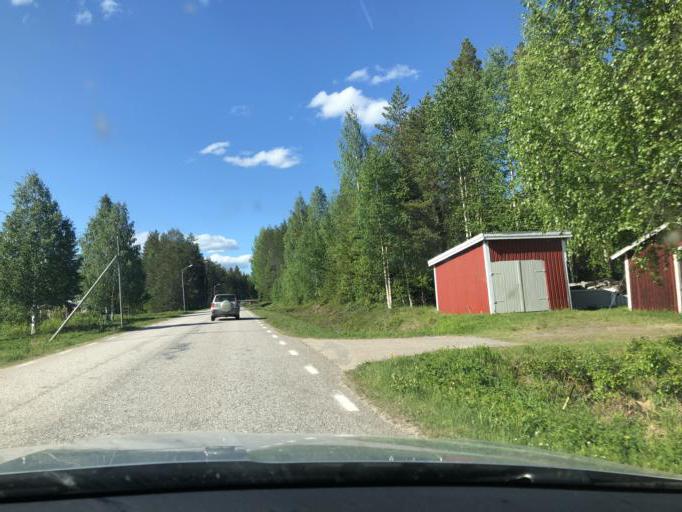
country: SE
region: Norrbotten
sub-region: Kalix Kommun
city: Kalix
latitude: 66.0102
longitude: 23.1426
